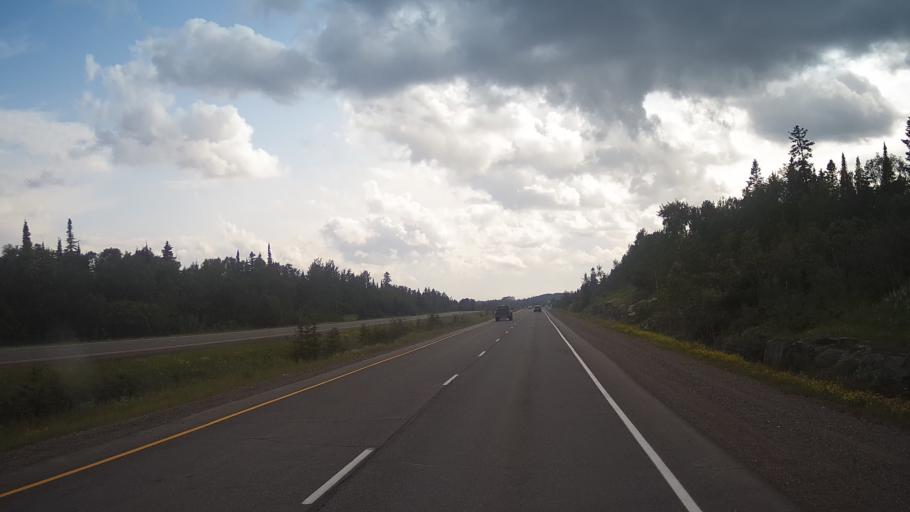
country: CA
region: Ontario
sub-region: Thunder Bay District
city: Thunder Bay
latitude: 48.4692
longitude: -89.2121
